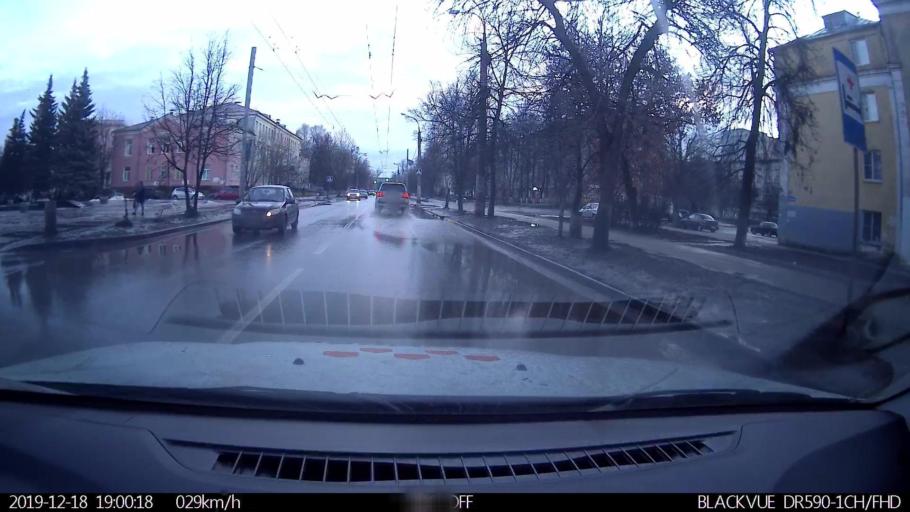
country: RU
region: Nizjnij Novgorod
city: Gorbatovka
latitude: 56.3296
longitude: 43.8495
